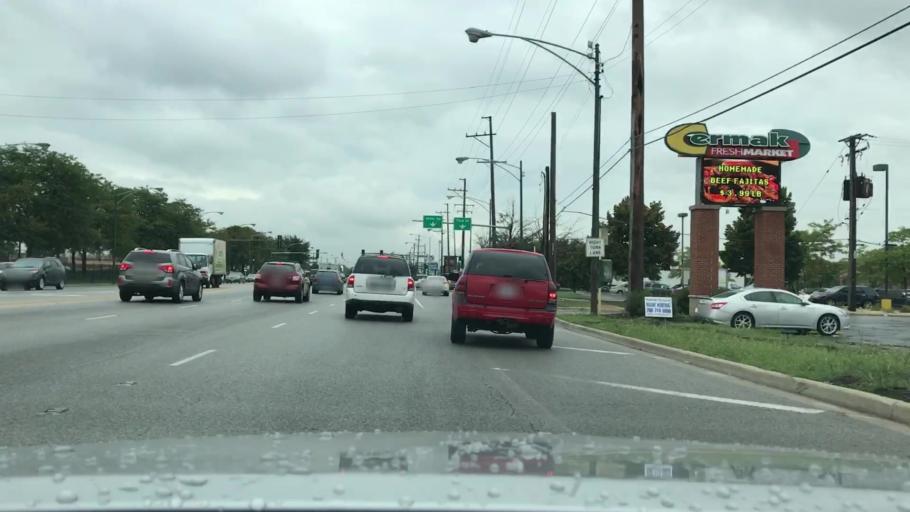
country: US
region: Illinois
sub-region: Cook County
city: Hometown
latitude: 41.7616
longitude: -87.7419
